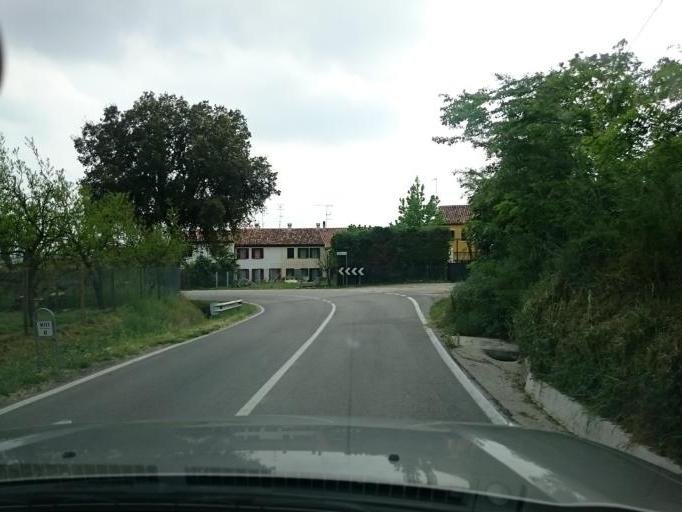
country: IT
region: Veneto
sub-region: Provincia di Padova
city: Este
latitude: 45.2331
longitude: 11.6596
